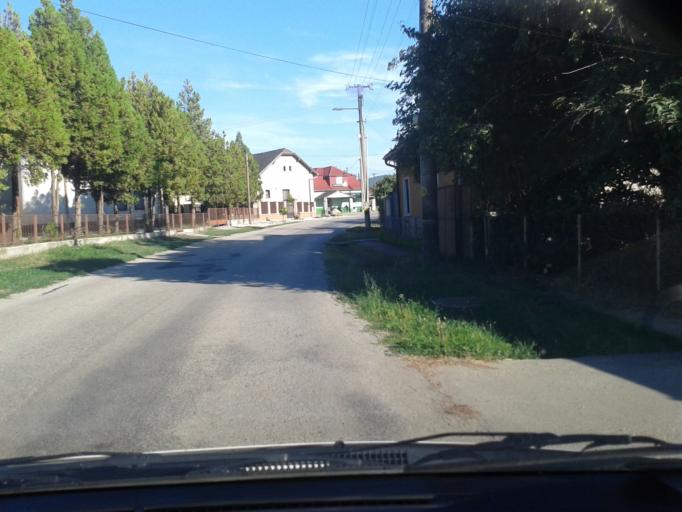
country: SK
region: Nitriansky
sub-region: Okres Nove Zamky
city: Sturovo
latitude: 47.8306
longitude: 18.7314
